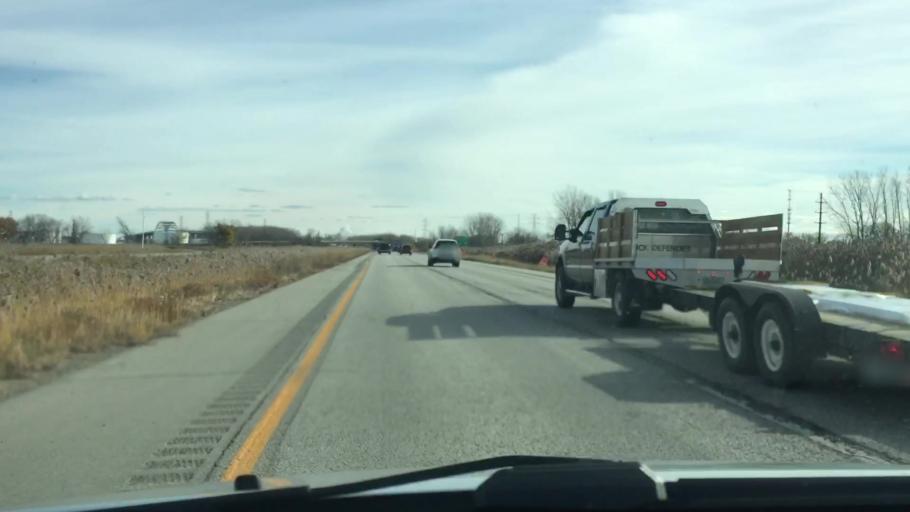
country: US
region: Wisconsin
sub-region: Brown County
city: Green Bay
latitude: 44.5448
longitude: -88.0322
